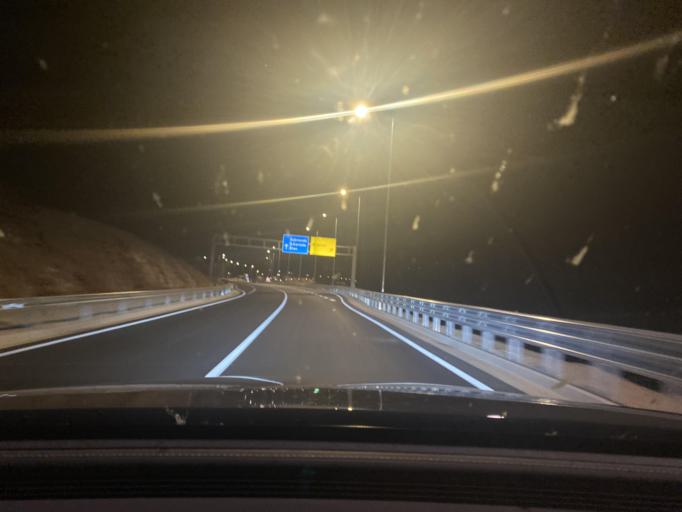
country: BA
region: Federation of Bosnia and Herzegovina
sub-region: Hercegovacko-Bosanski Kanton
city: Neum
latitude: 42.9089
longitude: 17.5324
